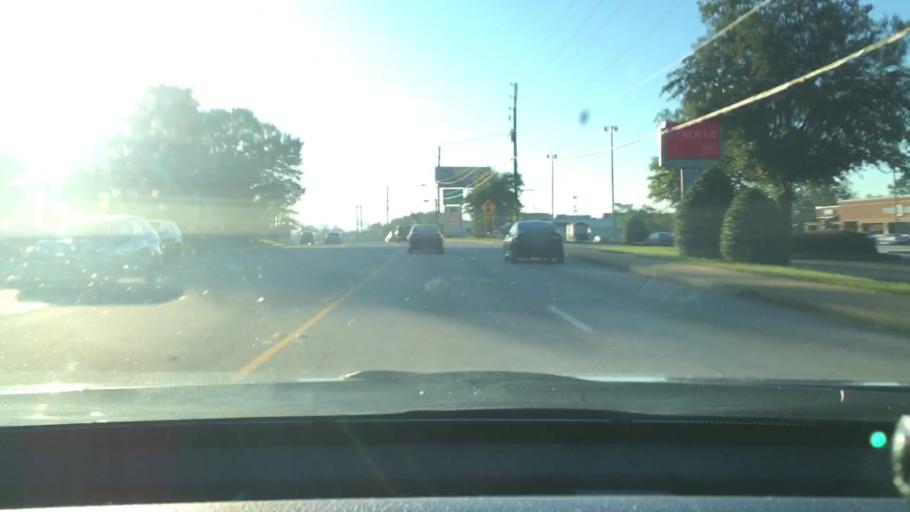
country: US
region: South Carolina
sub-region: Lexington County
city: West Columbia
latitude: 34.0260
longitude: -81.0819
